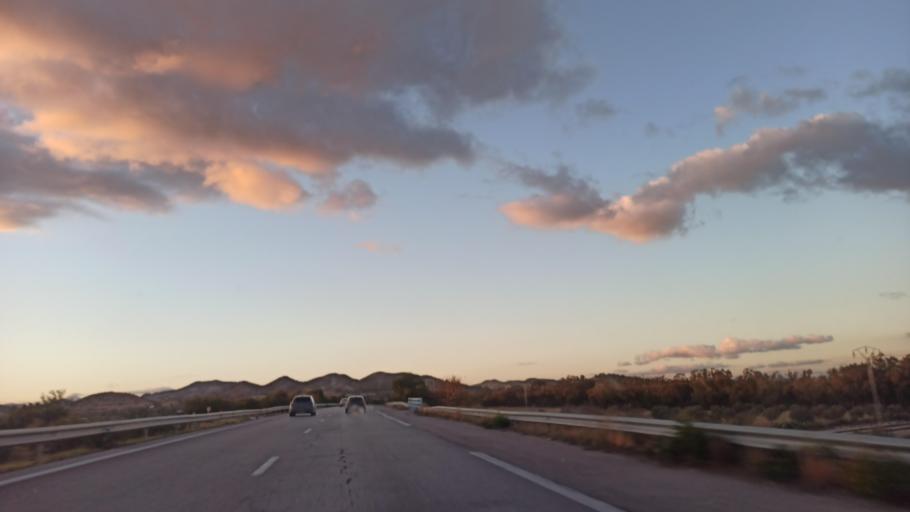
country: TN
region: Susah
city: Harqalah
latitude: 36.2137
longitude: 10.4229
